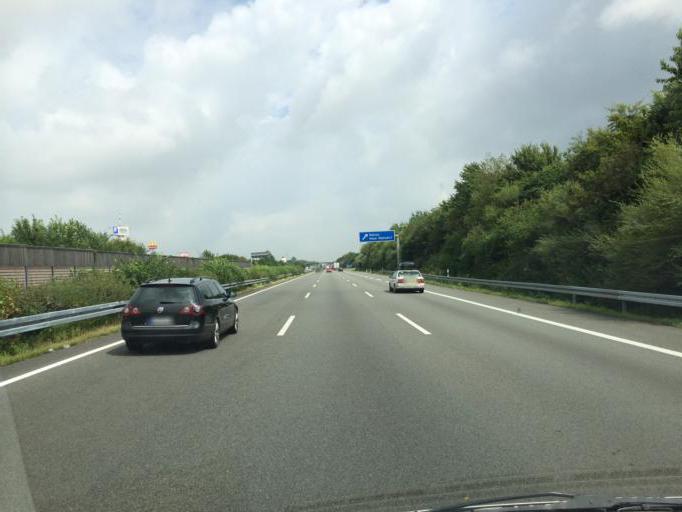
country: DE
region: Lower Saxony
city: Rehren
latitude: 52.2320
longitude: 9.2430
